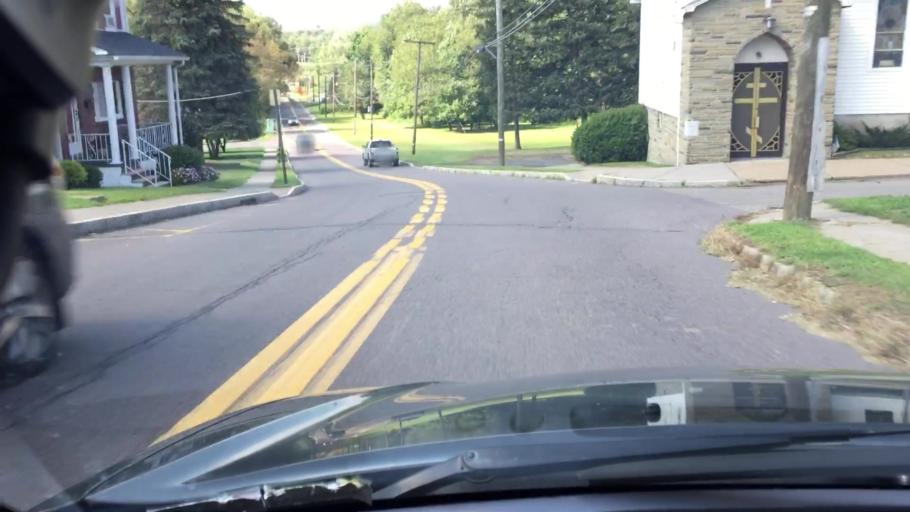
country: US
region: Pennsylvania
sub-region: Luzerne County
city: Nanticoke
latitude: 41.1865
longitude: -75.9867
